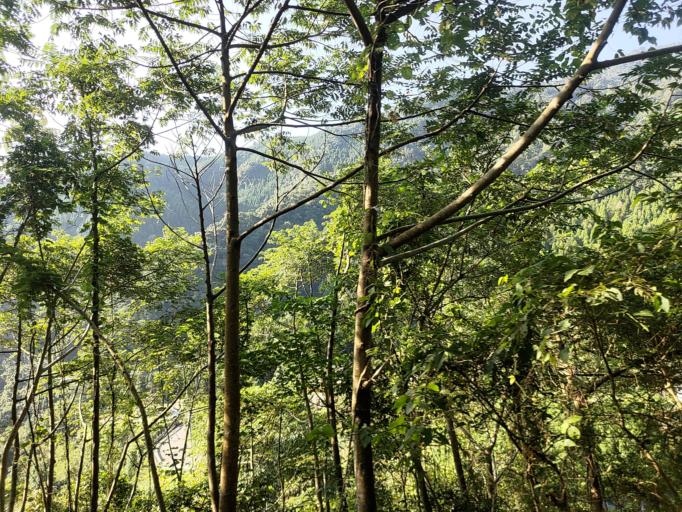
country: TW
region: Taiwan
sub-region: Hsinchu
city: Hsinchu
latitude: 24.6152
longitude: 121.0933
